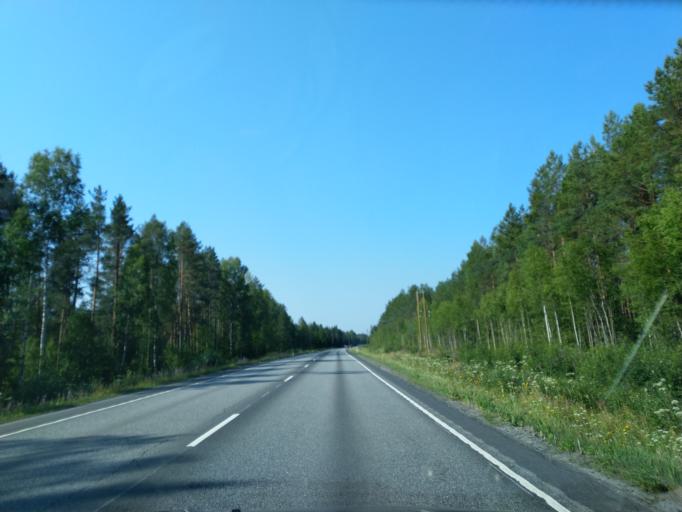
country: FI
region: Satakunta
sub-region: Pori
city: Pomarkku
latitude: 61.7124
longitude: 22.0384
